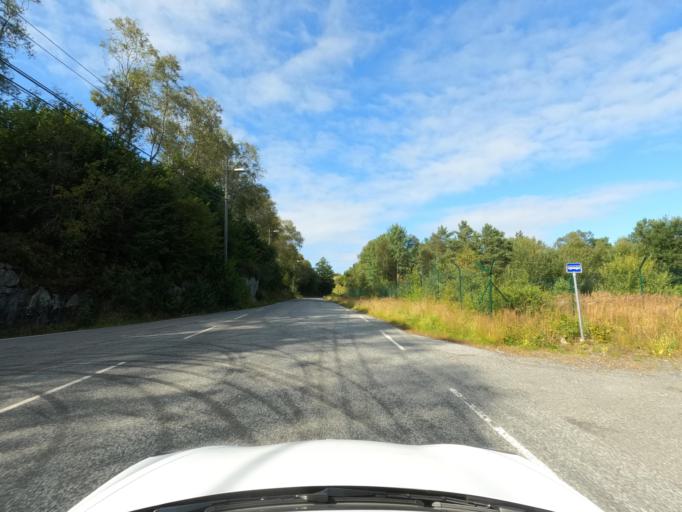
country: NO
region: Hordaland
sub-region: Bergen
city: Ytrebygda
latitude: 60.2839
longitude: 5.2171
